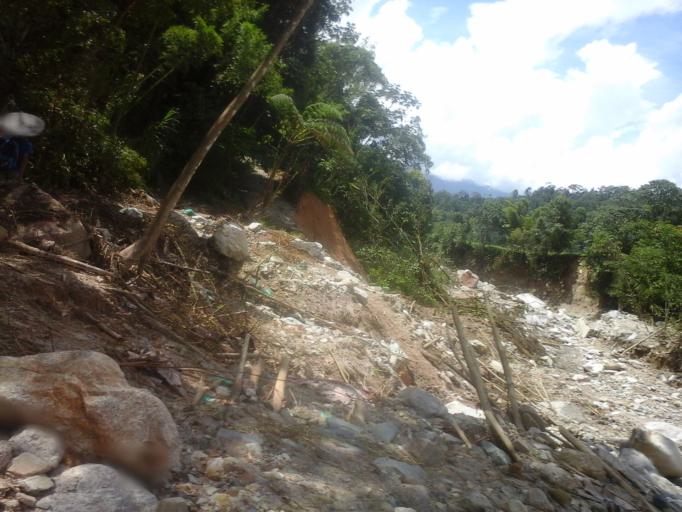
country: CO
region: Putumayo
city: Mocoa
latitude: 1.1831
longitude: -76.6773
